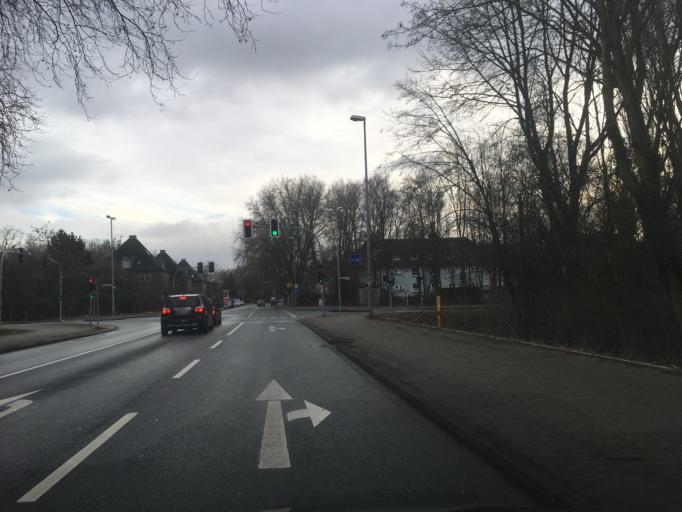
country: DE
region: North Rhine-Westphalia
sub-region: Regierungsbezirk Munster
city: Gelsenkirchen
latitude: 51.5403
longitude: 7.0859
